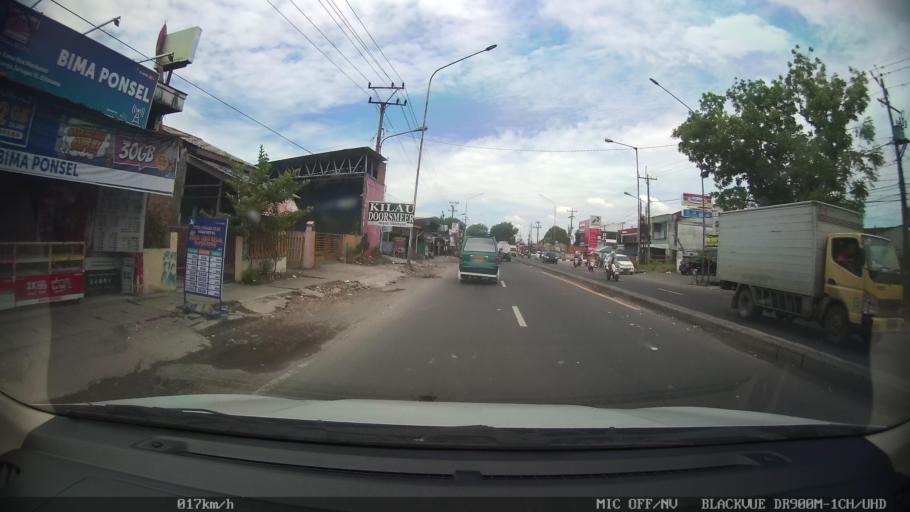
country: ID
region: North Sumatra
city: Sunggal
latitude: 3.5993
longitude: 98.5933
